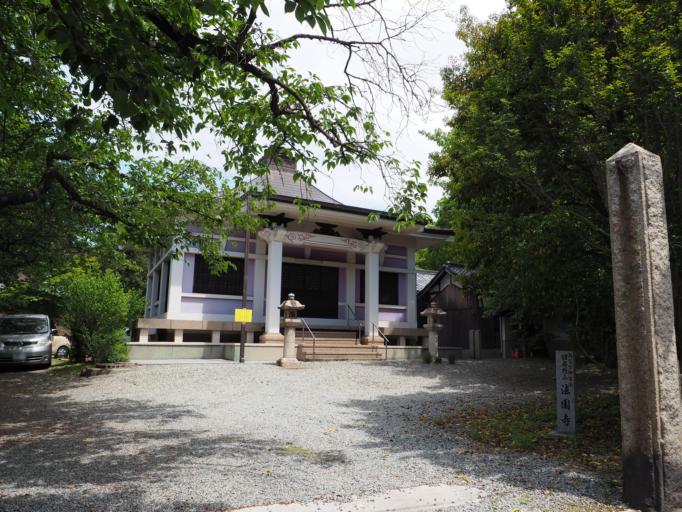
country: JP
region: Hyogo
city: Itami
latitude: 34.7681
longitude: 135.4257
